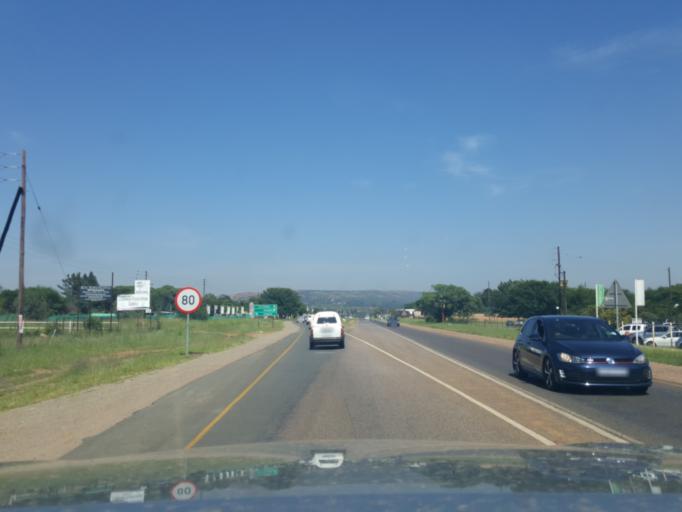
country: ZA
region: Gauteng
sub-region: City of Tshwane Metropolitan Municipality
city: Pretoria
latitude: -25.6817
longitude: 28.3086
